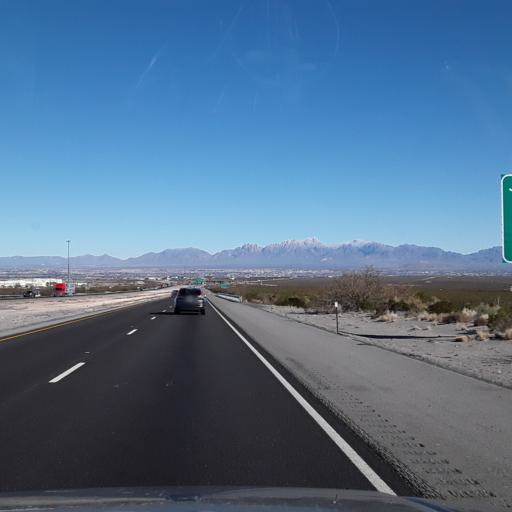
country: US
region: New Mexico
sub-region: Dona Ana County
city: Mesilla
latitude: 32.2764
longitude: -106.8996
